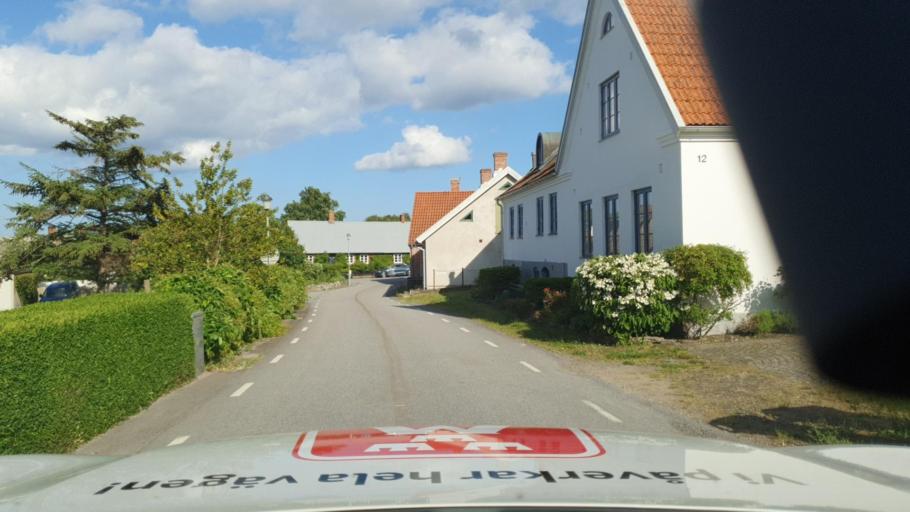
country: SE
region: Skane
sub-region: Simrishamns Kommun
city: Kivik
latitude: 55.6148
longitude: 14.2881
